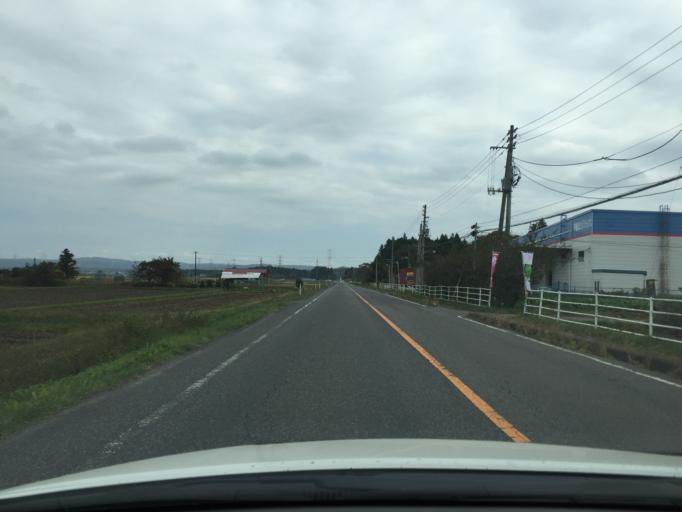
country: JP
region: Fukushima
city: Ishikawa
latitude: 37.0567
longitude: 140.3397
